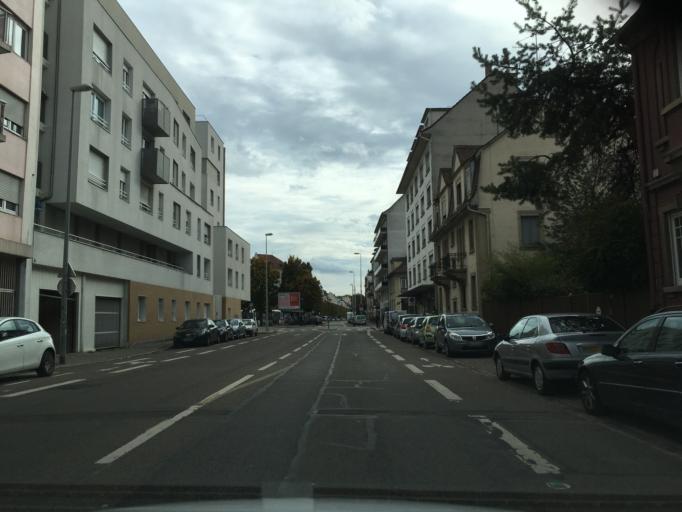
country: FR
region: Alsace
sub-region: Departement du Bas-Rhin
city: Strasbourg
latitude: 48.5697
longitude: 7.7511
